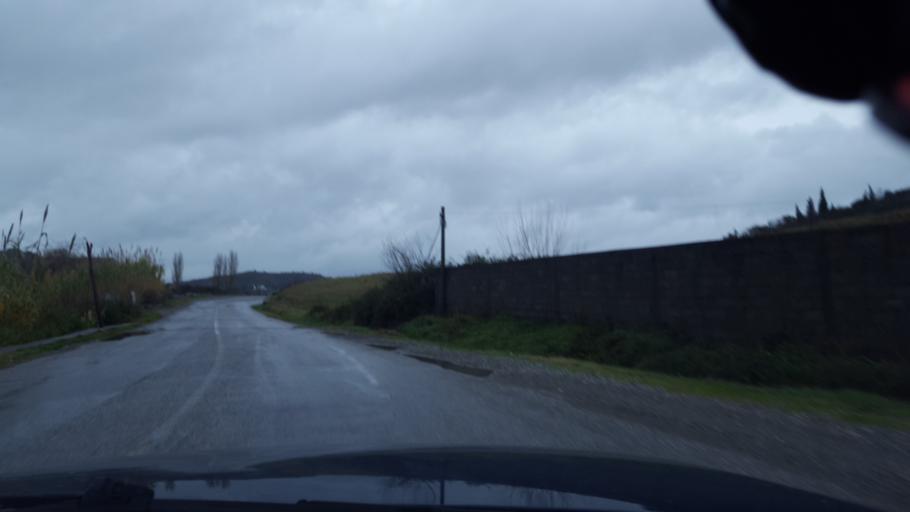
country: AL
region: Shkoder
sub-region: Rrethi i Shkodres
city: Berdica e Madhe
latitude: 42.0291
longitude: 19.4945
